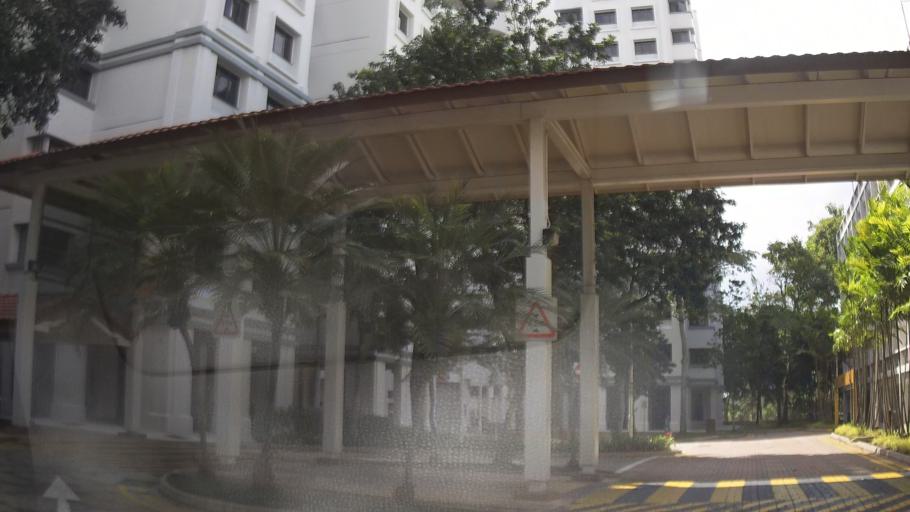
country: MY
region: Johor
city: Johor Bahru
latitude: 1.4040
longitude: 103.7460
